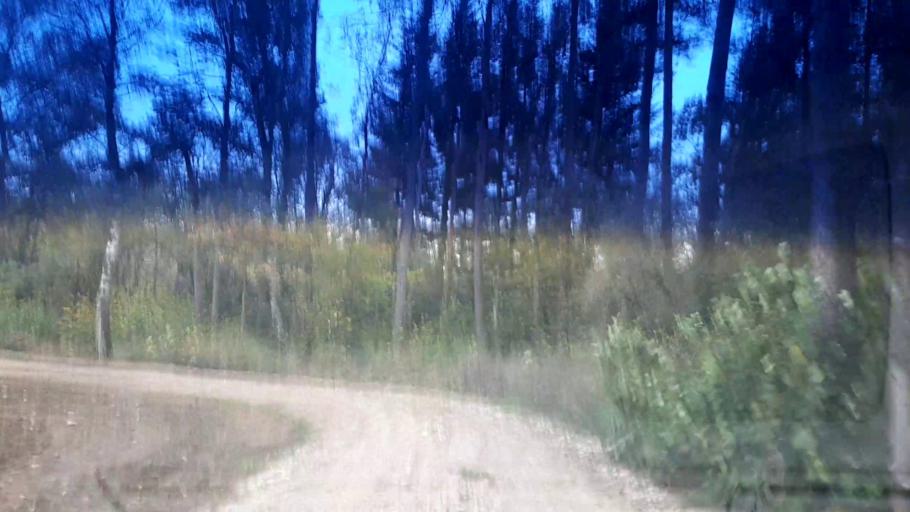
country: DE
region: Bavaria
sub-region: Upper Franconia
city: Poxdorf
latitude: 49.9331
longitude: 11.1019
